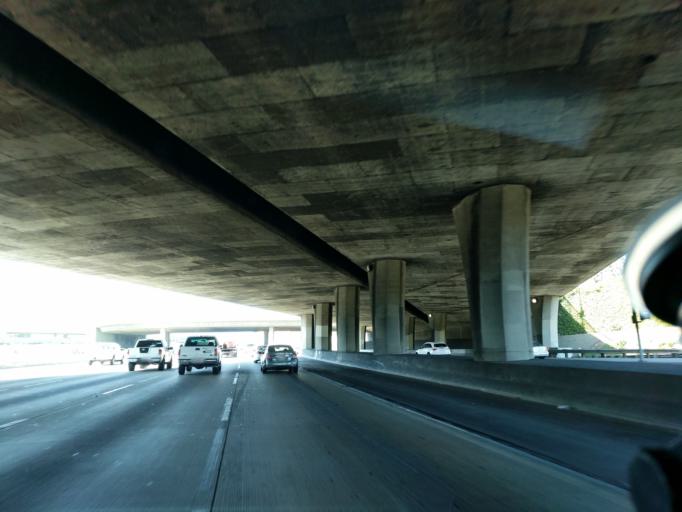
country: US
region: California
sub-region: Orange County
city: Santa Ana
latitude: 33.7682
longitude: -117.8673
